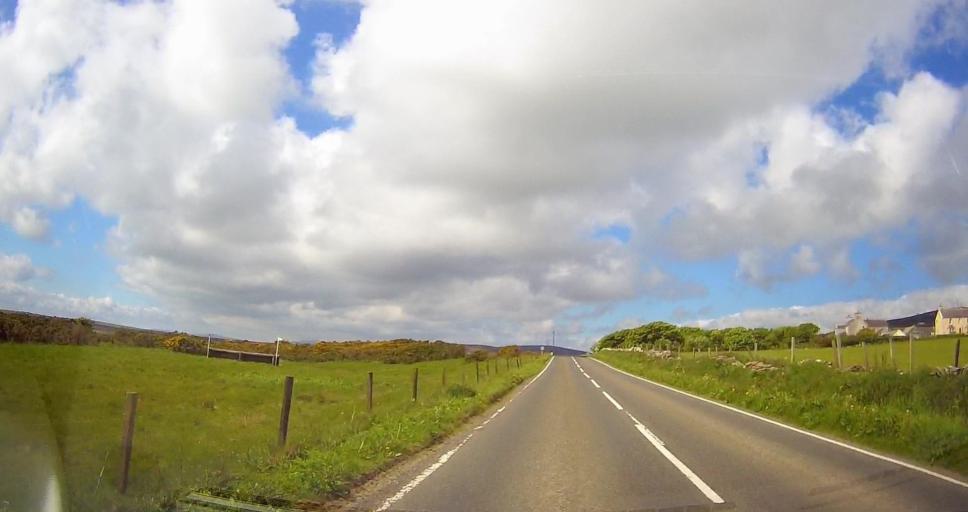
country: GB
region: Scotland
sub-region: Orkney Islands
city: Orkney
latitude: 58.9774
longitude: -2.9991
